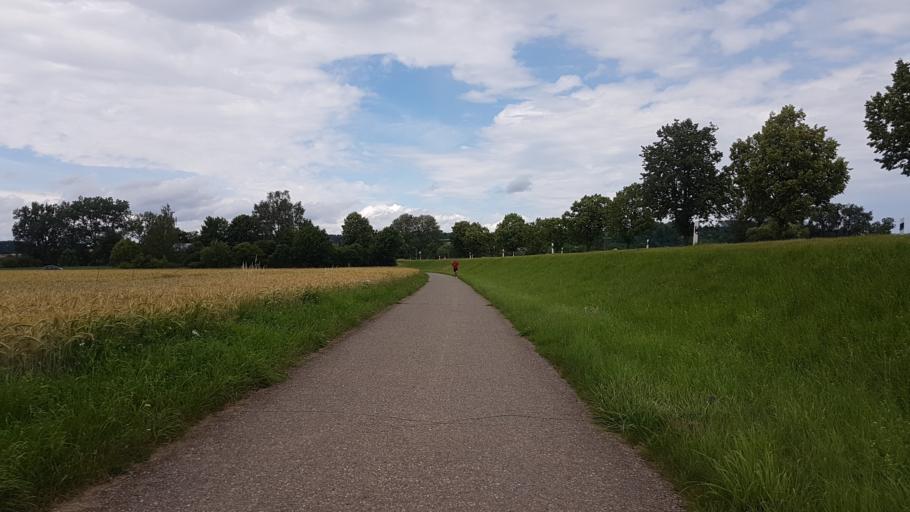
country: DE
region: Baden-Wuerttemberg
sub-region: Tuebingen Region
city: Mengen
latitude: 48.0603
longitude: 9.3461
